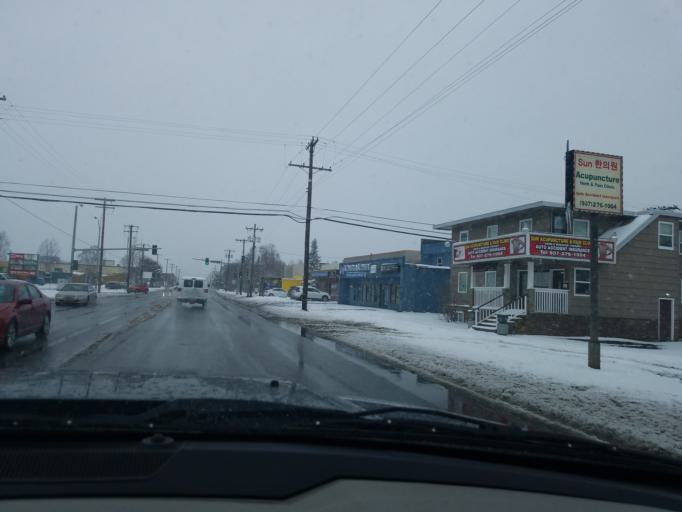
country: US
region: Alaska
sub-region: Anchorage Municipality
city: Anchorage
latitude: 61.1980
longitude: -149.8750
